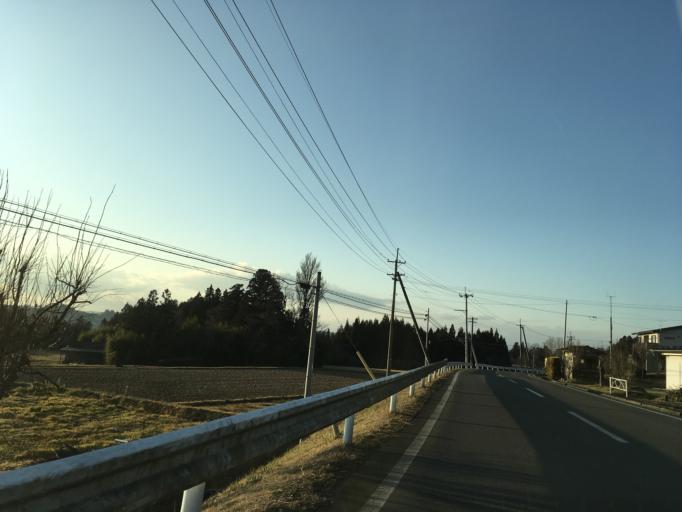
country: JP
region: Iwate
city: Ichinoseki
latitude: 38.8202
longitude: 141.2132
